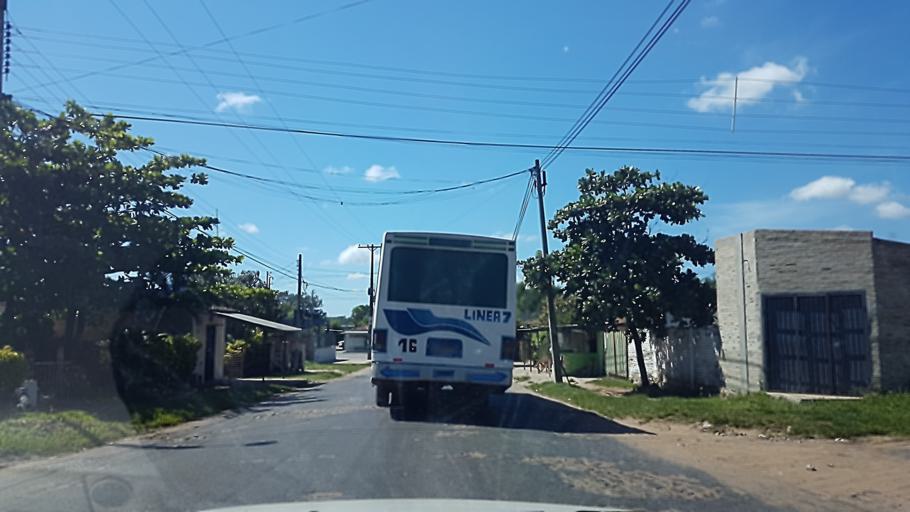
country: PY
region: Central
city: Colonia Mariano Roque Alonso
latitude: -25.2179
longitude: -57.5208
